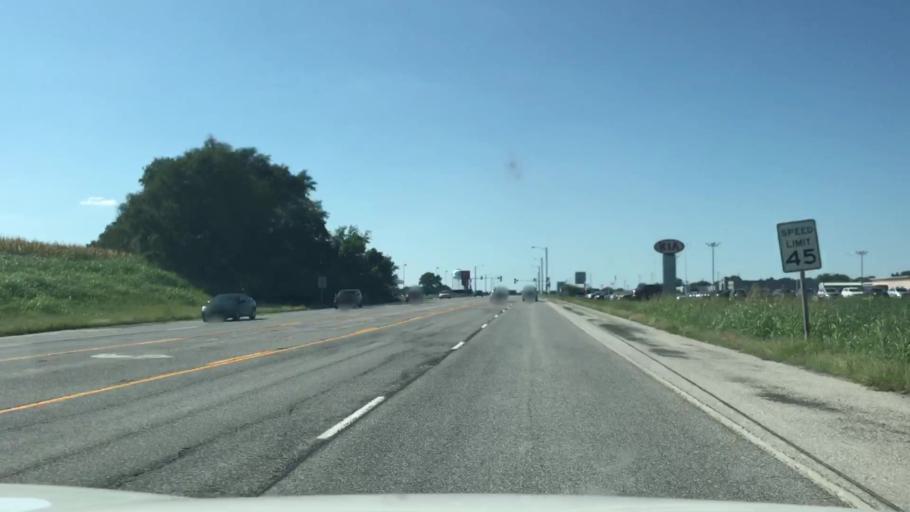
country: US
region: Illinois
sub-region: Madison County
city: Roxana
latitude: 38.8557
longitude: -90.0626
